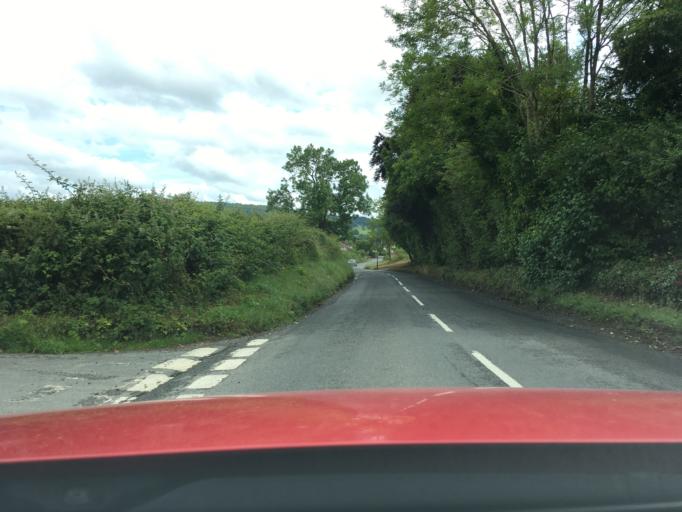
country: GB
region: England
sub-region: Gloucestershire
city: Winchcombe
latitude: 51.9705
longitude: -1.9678
